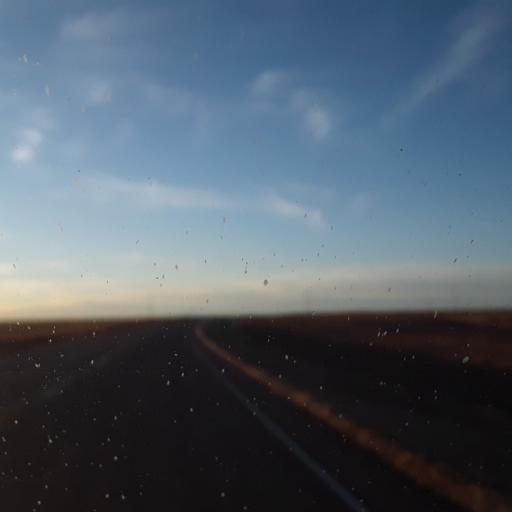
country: US
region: Colorado
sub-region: Cheyenne County
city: Cheyenne Wells
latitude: 38.8086
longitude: -102.4219
